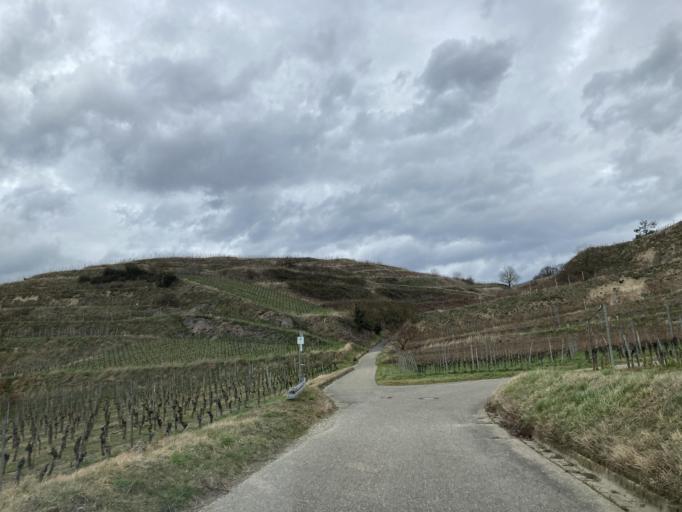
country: DE
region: Baden-Wuerttemberg
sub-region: Freiburg Region
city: Vogtsburg
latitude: 48.1079
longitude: 7.6364
